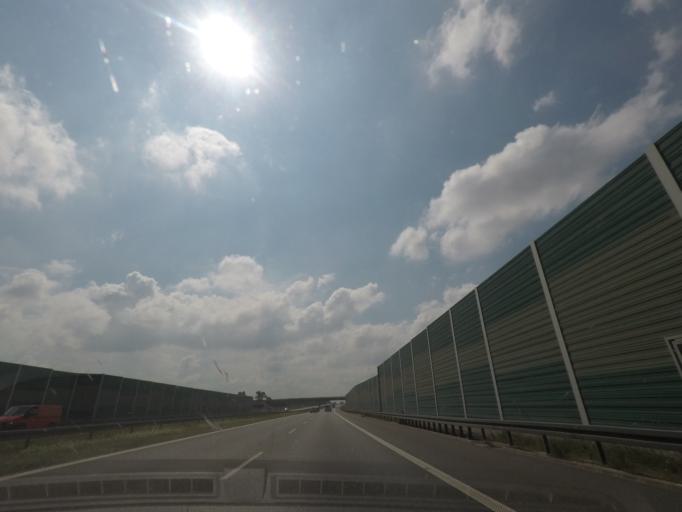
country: PL
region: Lodz Voivodeship
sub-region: Powiat kutnowski
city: Krzyzanow
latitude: 52.2026
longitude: 19.4844
